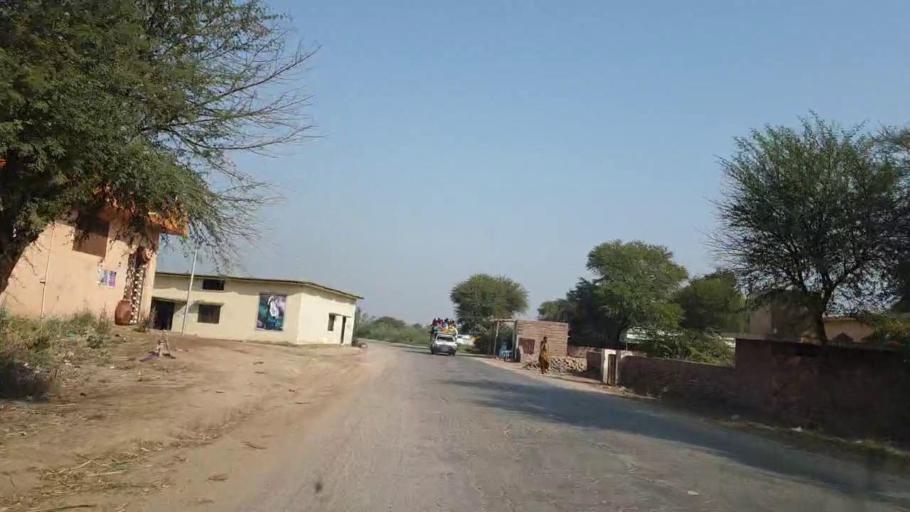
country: PK
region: Sindh
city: Mirpur Khas
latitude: 25.5355
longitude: 69.0455
